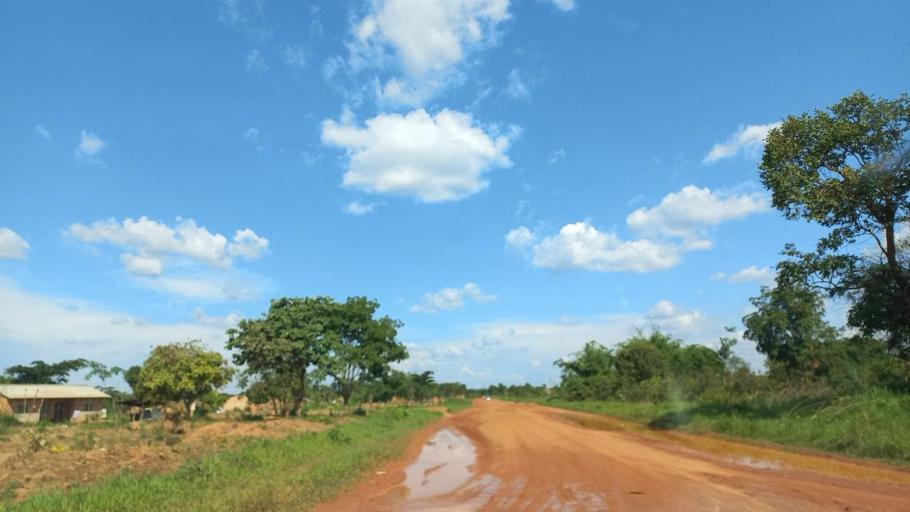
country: ZM
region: Copperbelt
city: Kitwe
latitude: -12.8701
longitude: 28.3571
